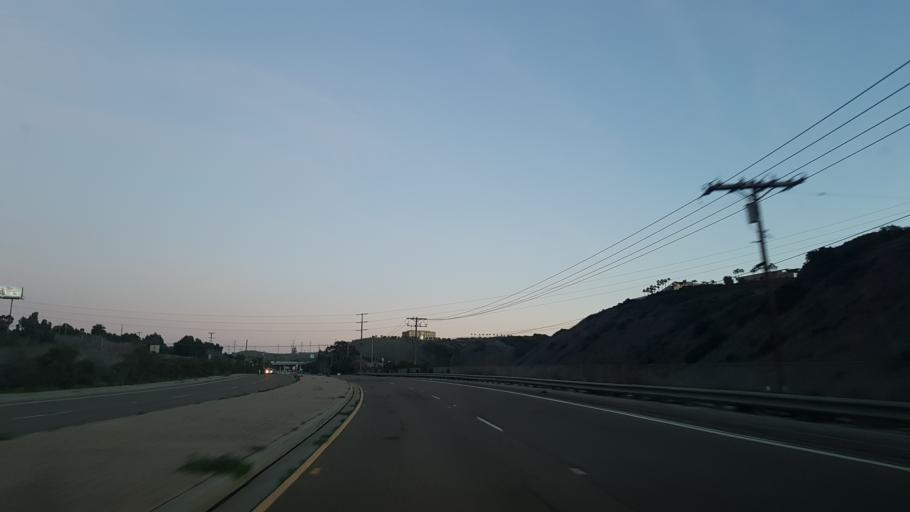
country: US
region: California
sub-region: San Diego County
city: La Jolla
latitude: 32.8933
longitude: -117.2156
